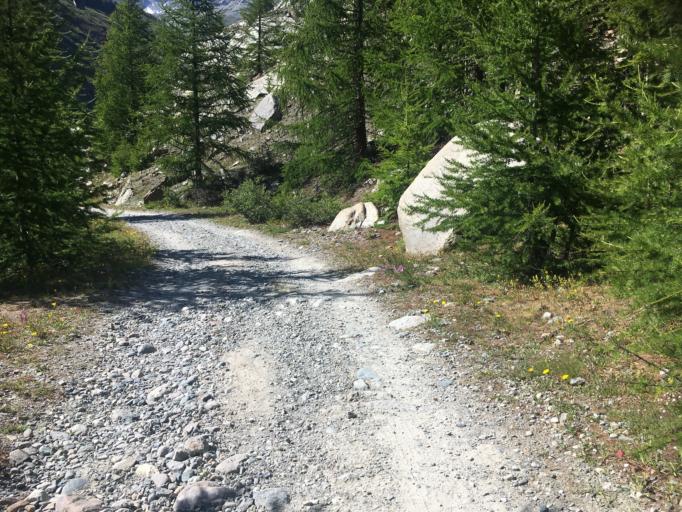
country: CH
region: Valais
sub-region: Visp District
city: Zermatt
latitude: 45.9914
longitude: 7.7309
